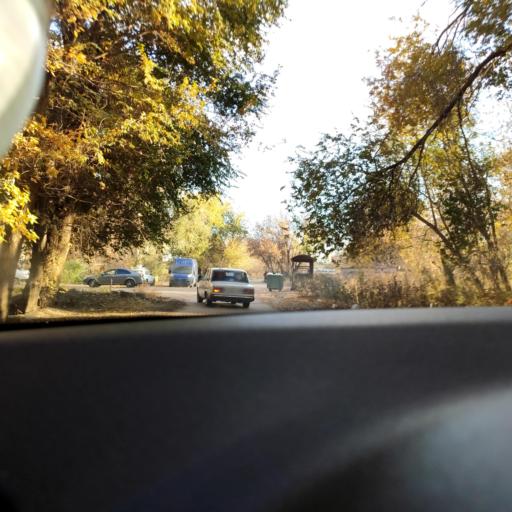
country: RU
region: Samara
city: Samara
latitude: 53.2142
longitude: 50.2657
